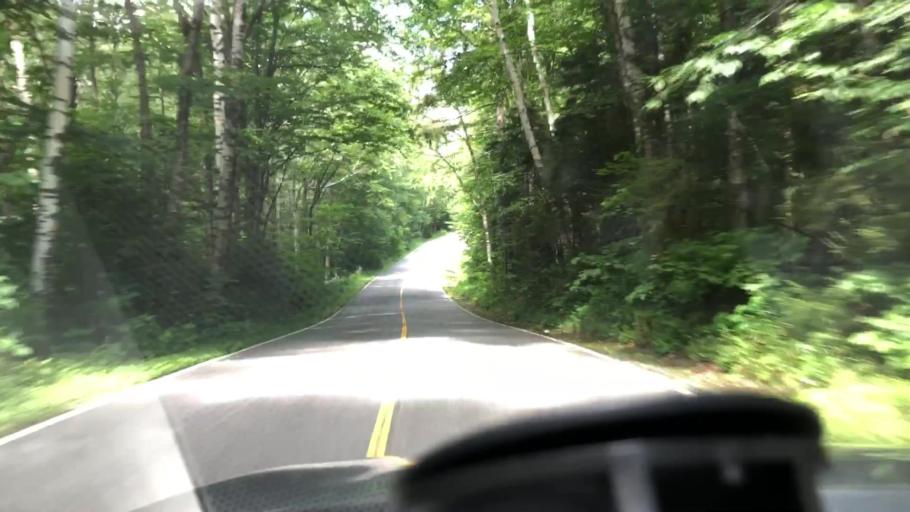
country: US
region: Massachusetts
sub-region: Berkshire County
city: Williamstown
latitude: 42.6680
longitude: -73.1669
